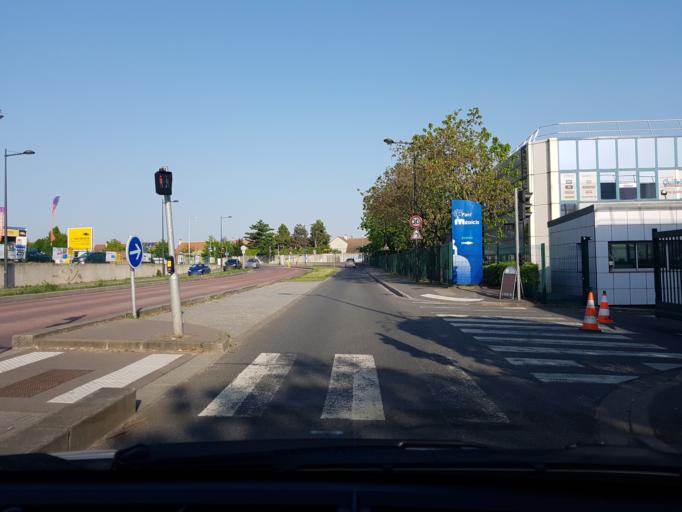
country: FR
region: Ile-de-France
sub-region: Departement du Val-de-Marne
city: Rungis
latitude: 48.7536
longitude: 2.3399
